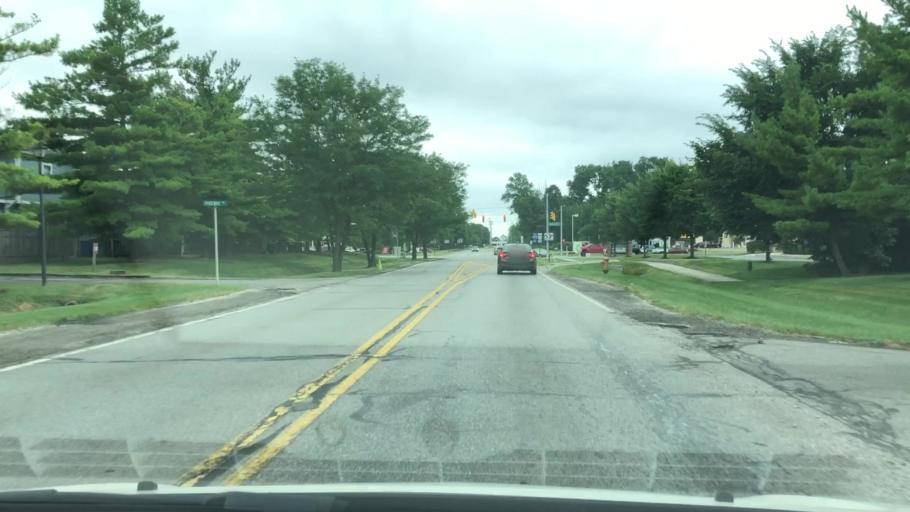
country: US
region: Ohio
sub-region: Franklin County
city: Worthington
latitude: 40.1200
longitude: -82.9954
